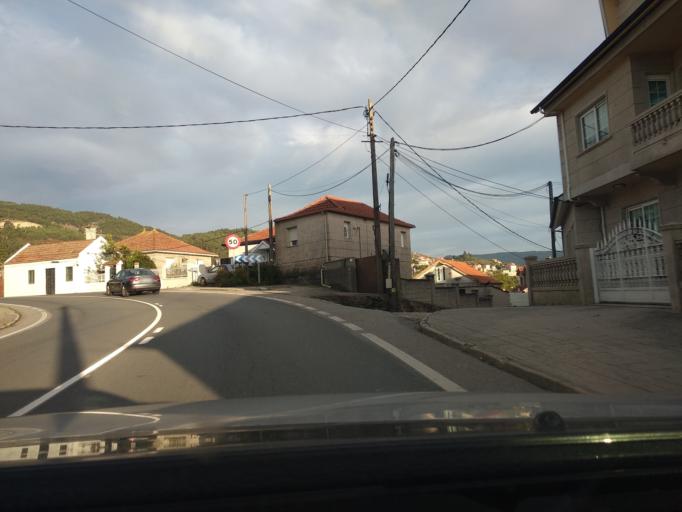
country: ES
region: Galicia
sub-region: Provincia de Pontevedra
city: Moana
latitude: 42.2863
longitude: -8.7229
